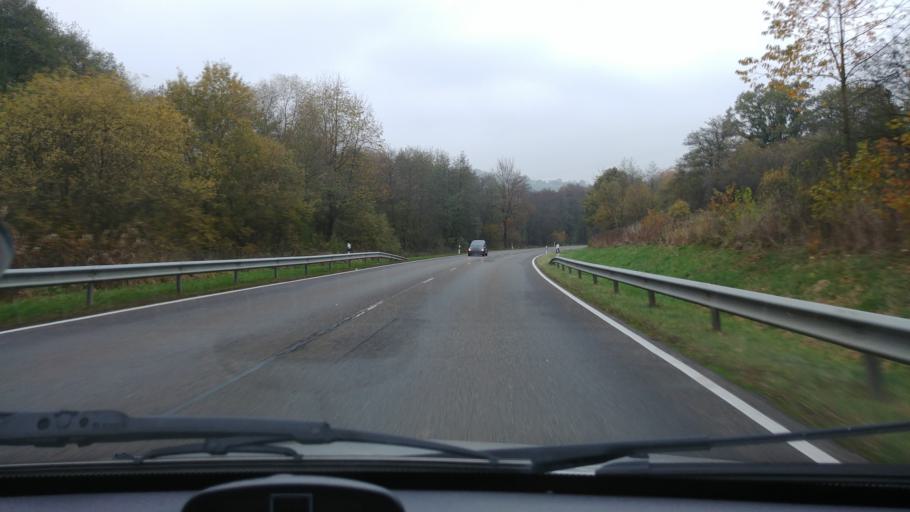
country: DE
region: Rheinland-Pfalz
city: Enspel
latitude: 50.6149
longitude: 7.8815
